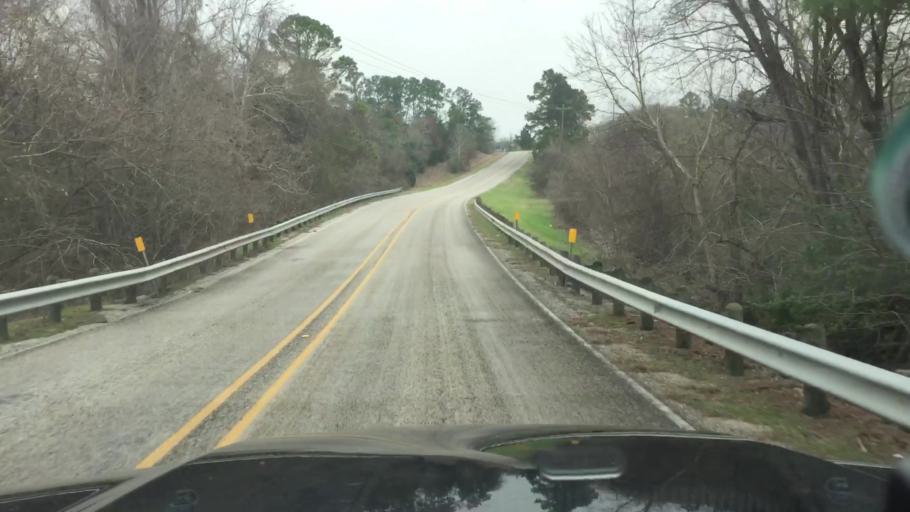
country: US
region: Texas
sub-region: Fayette County
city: La Grange
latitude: 30.0018
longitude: -96.8975
